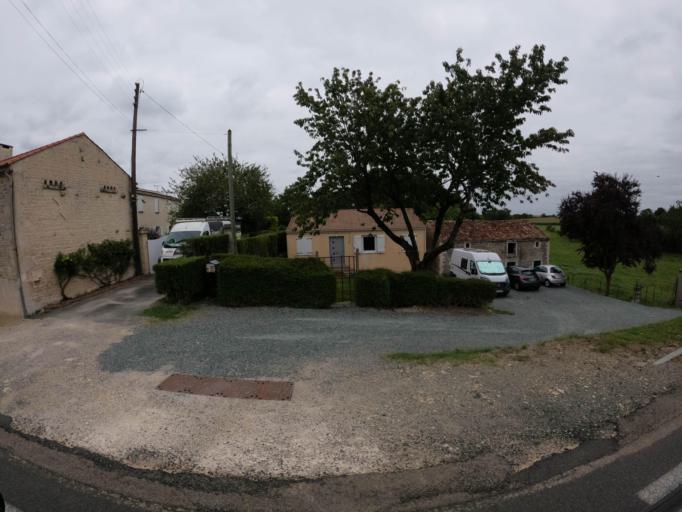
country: FR
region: Pays de la Loire
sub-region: Departement de la Vendee
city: Saint-Hilaire-des-Loges
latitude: 46.4035
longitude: -0.6728
